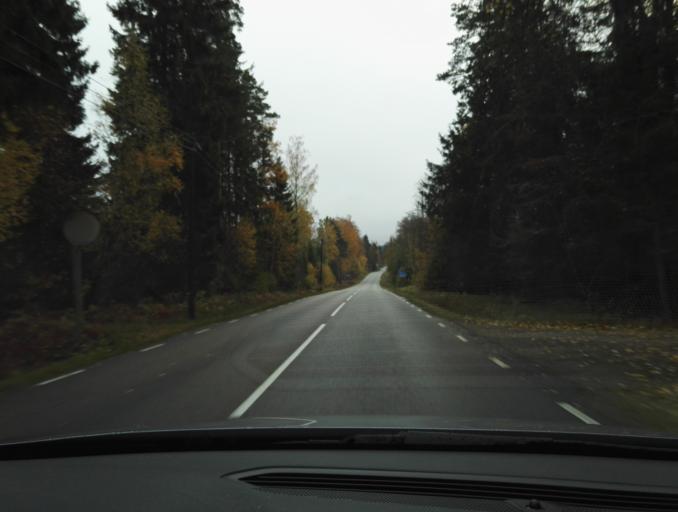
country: SE
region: Kronoberg
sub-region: Vaxjo Kommun
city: Rottne
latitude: 57.0317
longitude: 14.8095
